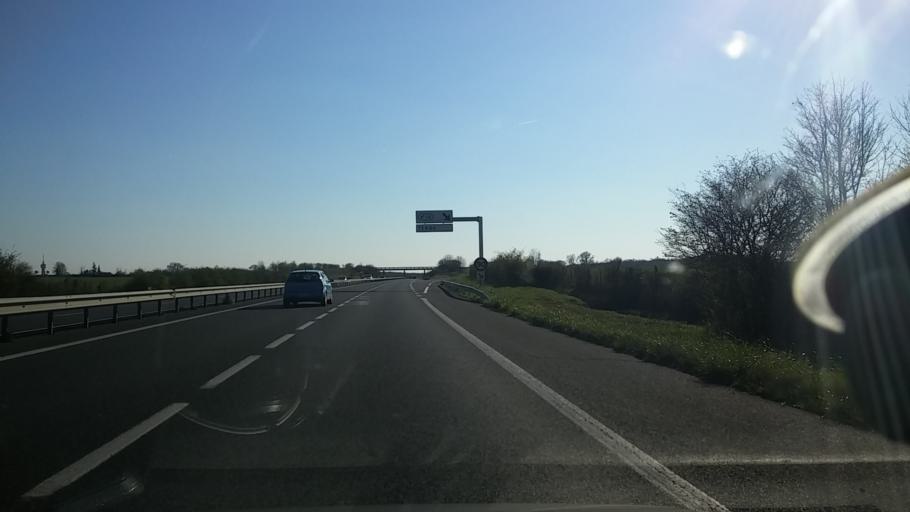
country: FR
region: Centre
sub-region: Departement de l'Indre
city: Saint-Marcel
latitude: 46.6543
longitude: 1.5656
